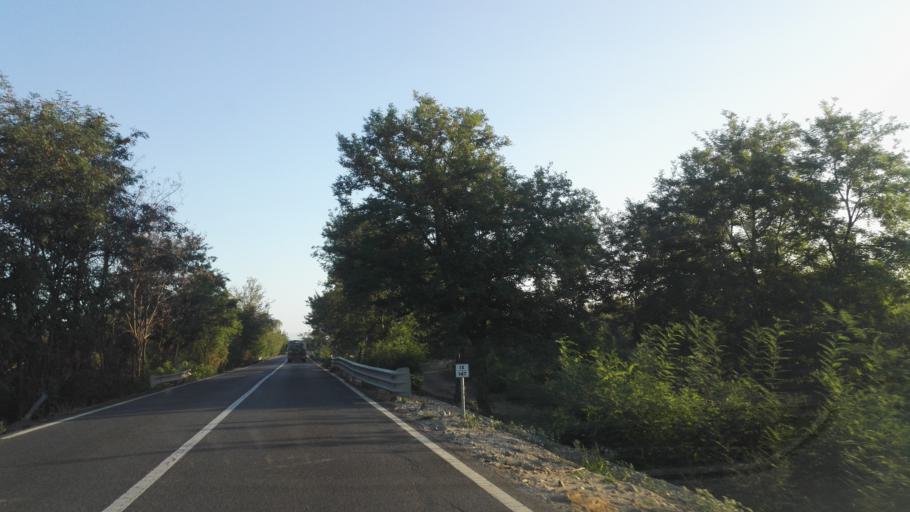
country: IT
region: Calabria
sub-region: Provincia di Catanzaro
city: Santa Caterina dello Ionio Marina
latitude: 38.5470
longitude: 16.5700
